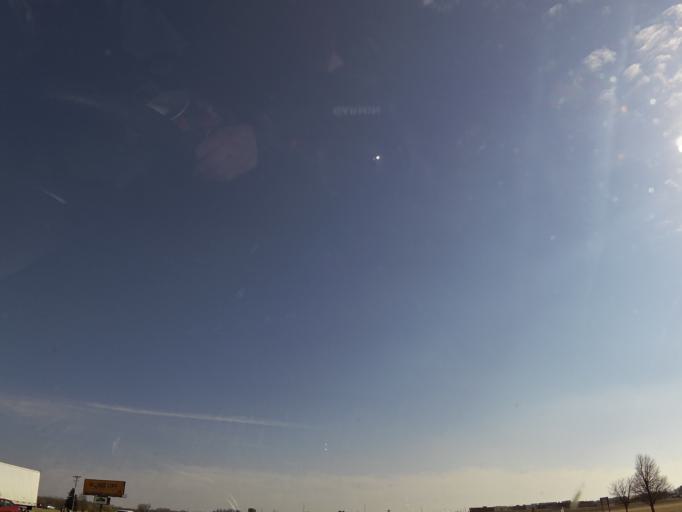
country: US
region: Minnesota
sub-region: Steele County
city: Owatonna
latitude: 44.1205
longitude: -93.2471
